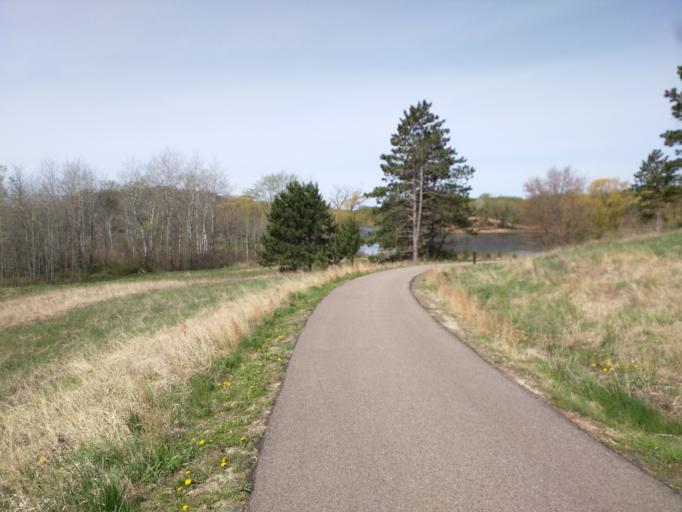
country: US
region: Minnesota
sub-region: Dakota County
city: Rosemount
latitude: 44.6843
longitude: -93.0823
